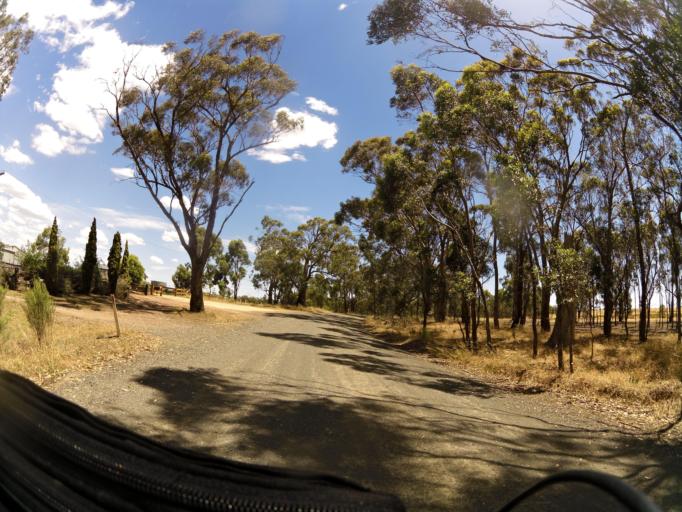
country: AU
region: Victoria
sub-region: Campaspe
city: Kyabram
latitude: -36.7942
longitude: 145.0848
